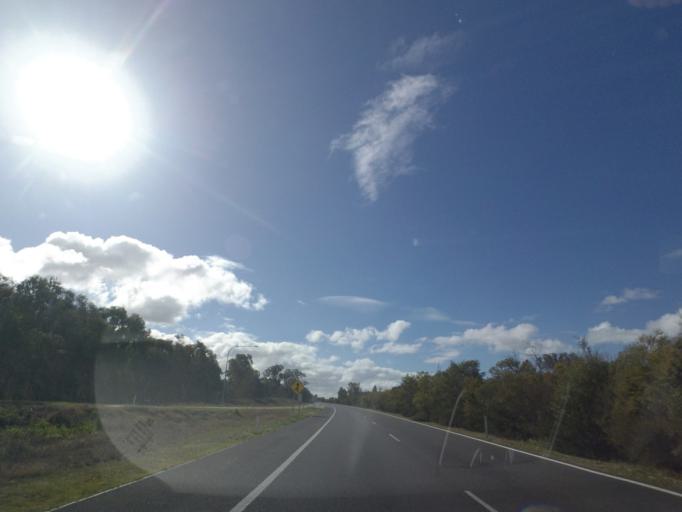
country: AU
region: New South Wales
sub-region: Albury Municipality
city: Lavington
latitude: -36.0374
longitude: 146.9748
